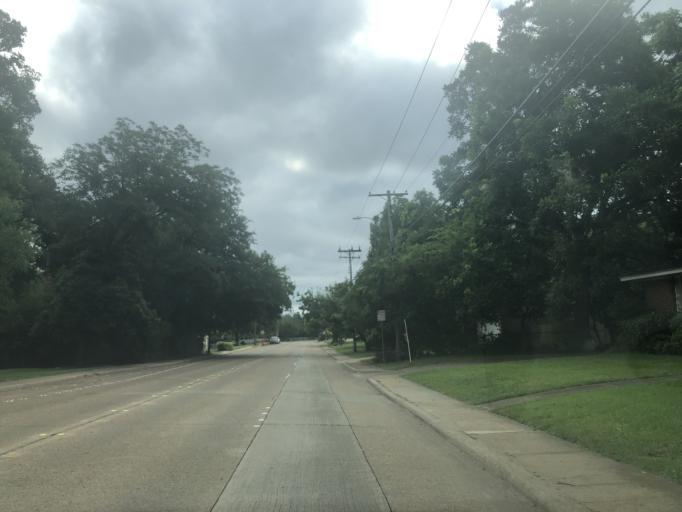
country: US
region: Texas
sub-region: Dallas County
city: Duncanville
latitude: 32.6517
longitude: -96.9057
